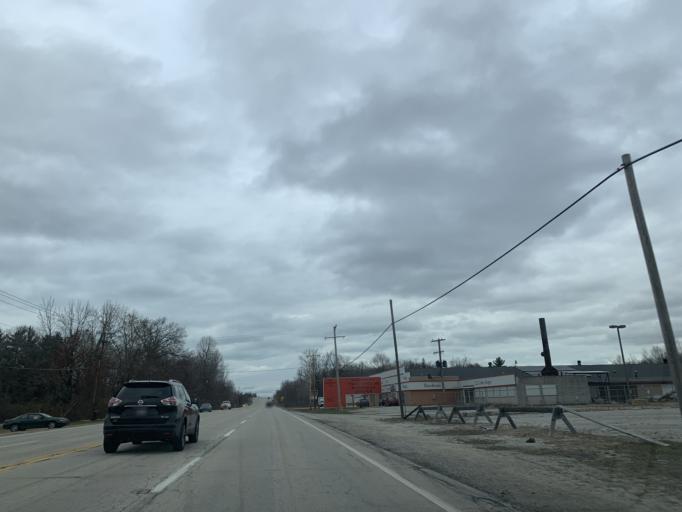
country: US
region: Indiana
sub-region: LaPorte County
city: Trail Creek
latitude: 41.7096
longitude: -86.8259
